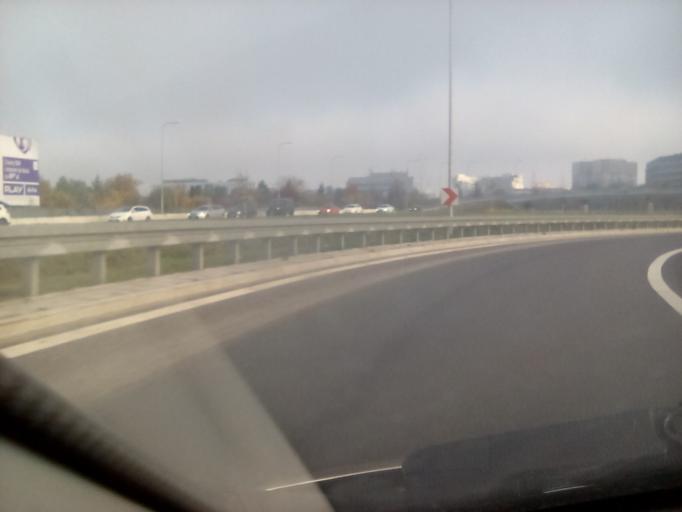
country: PL
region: Masovian Voivodeship
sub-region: Warszawa
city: Wlochy
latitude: 52.1829
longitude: 20.9837
